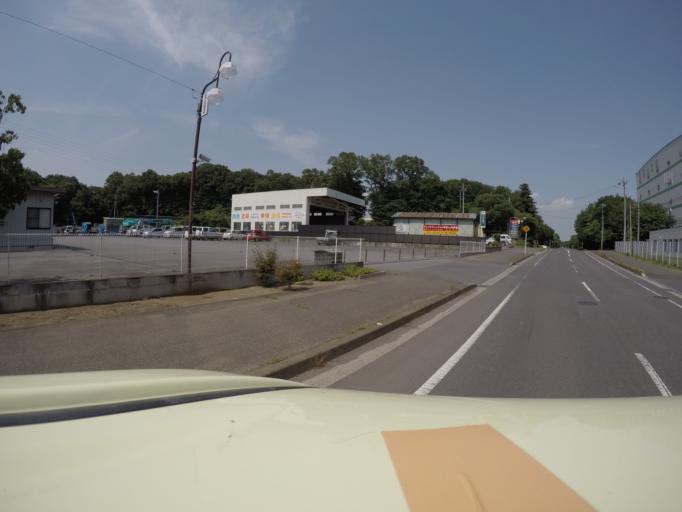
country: JP
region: Ibaraki
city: Iwai
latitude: 36.0534
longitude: 139.9131
